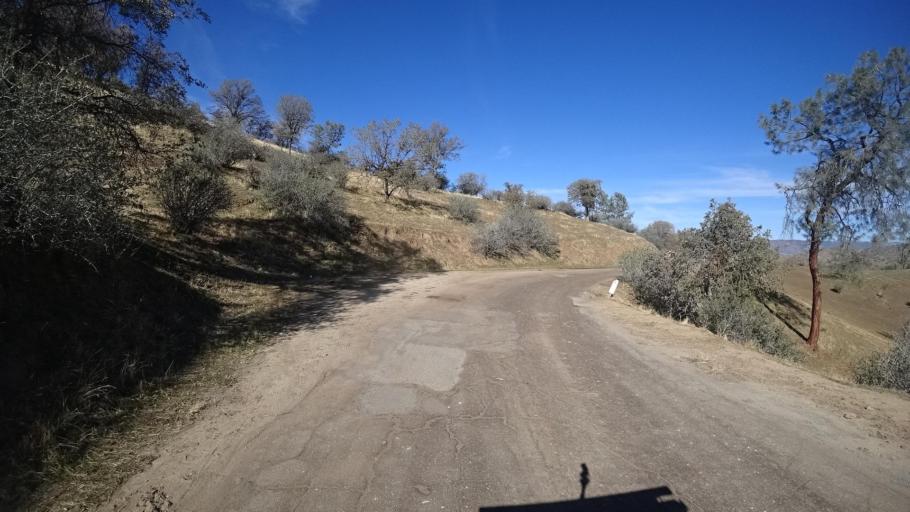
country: US
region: California
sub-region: Kern County
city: Bodfish
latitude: 35.4420
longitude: -118.7059
